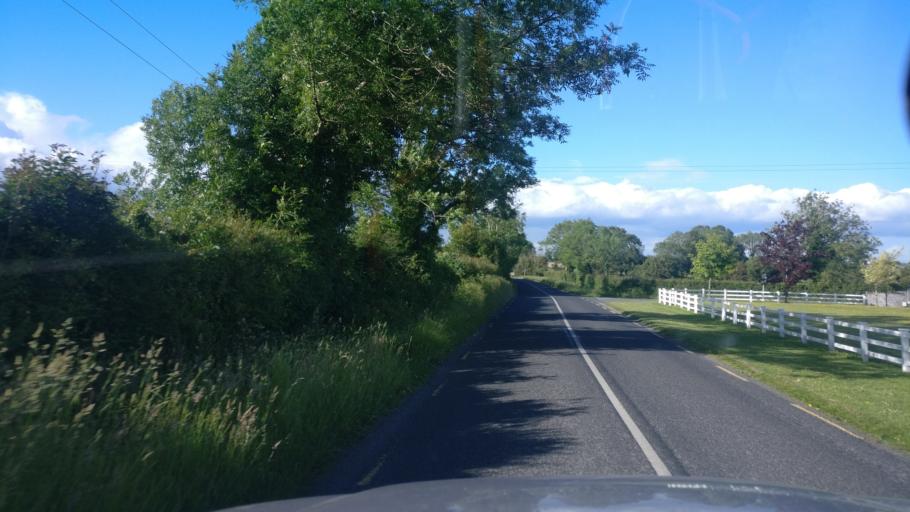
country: IE
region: Connaught
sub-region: County Galway
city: Ballinasloe
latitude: 53.2085
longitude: -8.2987
